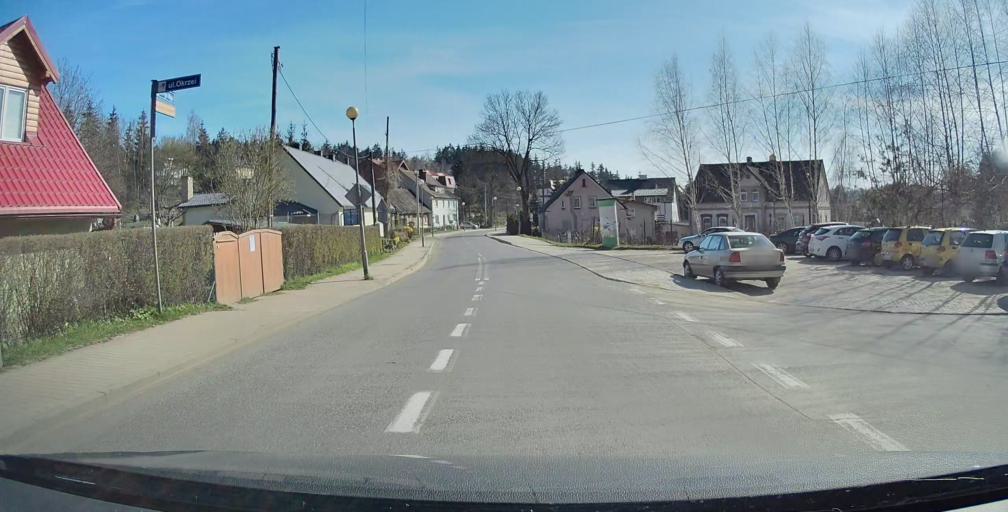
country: PL
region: Lower Silesian Voivodeship
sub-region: Powiat klodzki
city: Kudowa-Zdroj
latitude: 50.4454
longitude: 16.2553
